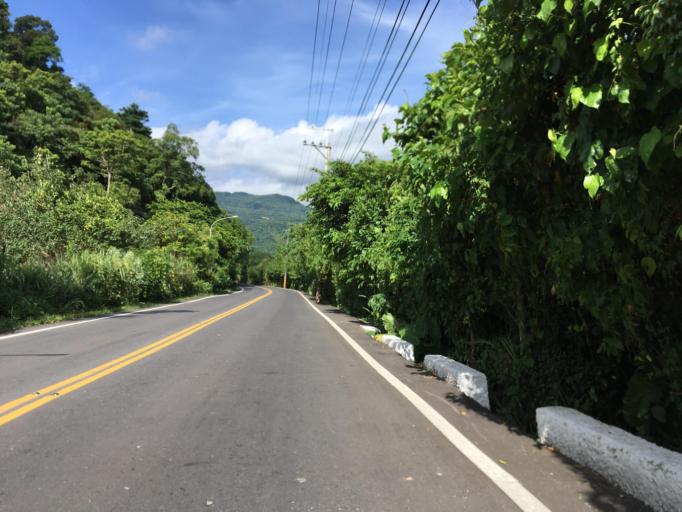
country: TW
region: Taiwan
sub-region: Yilan
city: Yilan
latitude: 24.6197
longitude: 121.7002
